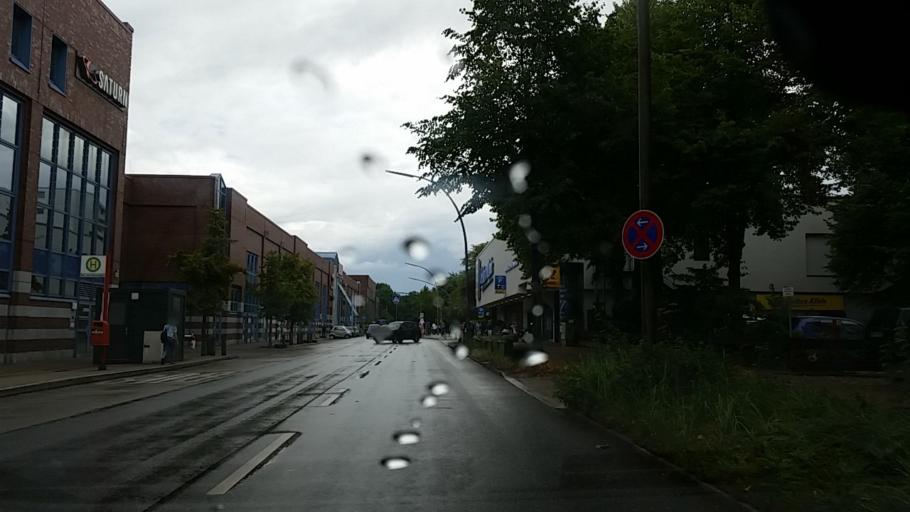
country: DE
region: Hamburg
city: Eidelstedt
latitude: 53.5700
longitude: 9.8605
